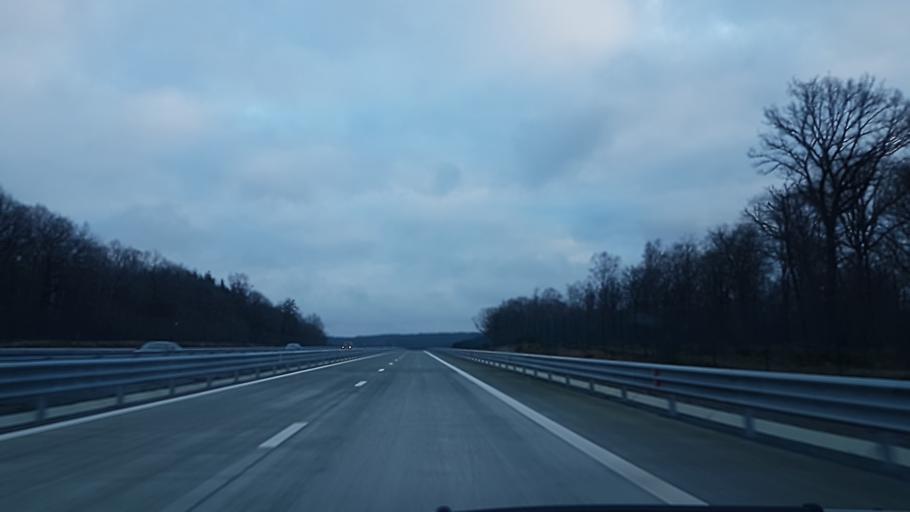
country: BE
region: Wallonia
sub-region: Province de Namur
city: Couvin
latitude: 50.0190
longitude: 4.5278
